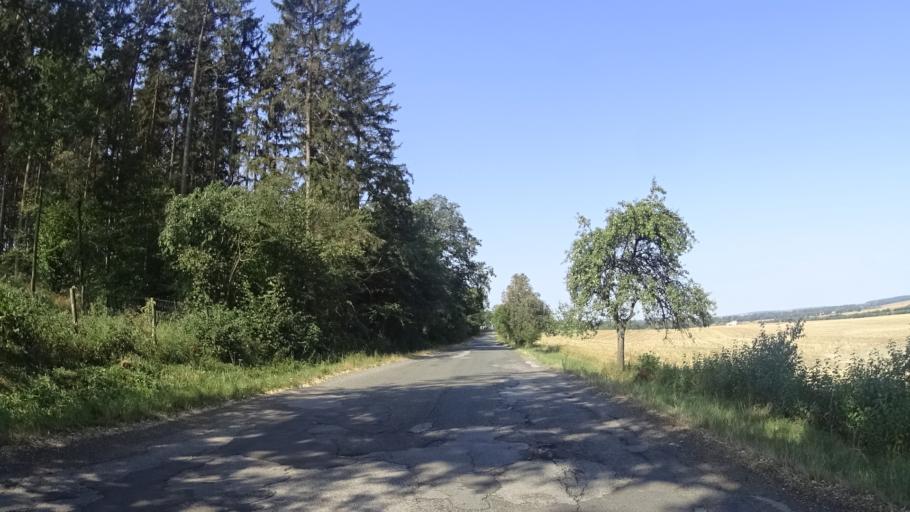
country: CZ
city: Smidary
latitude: 50.2800
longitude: 15.5282
